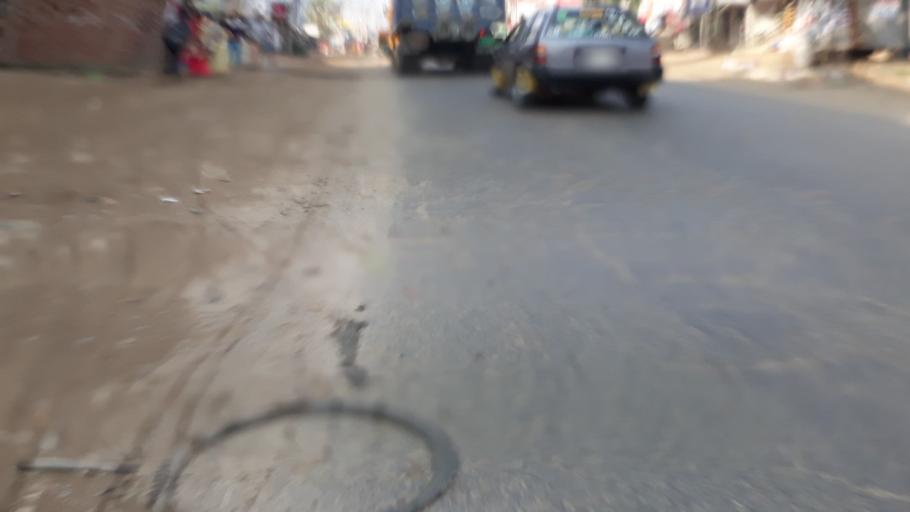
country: BD
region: Dhaka
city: Tungi
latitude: 23.9115
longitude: 90.3201
